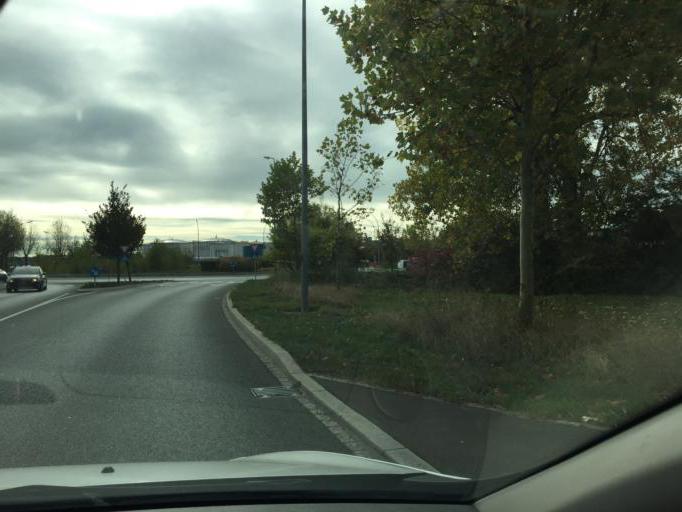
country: LU
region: Luxembourg
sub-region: Canton de Luxembourg
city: Strassen
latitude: 49.6116
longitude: 6.0705
